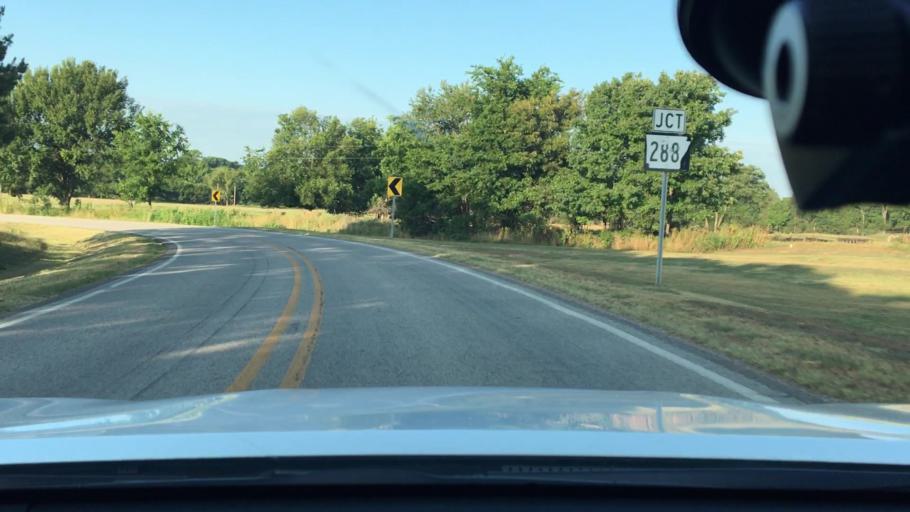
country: US
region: Arkansas
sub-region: Johnson County
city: Coal Hill
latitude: 35.3395
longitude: -93.6036
